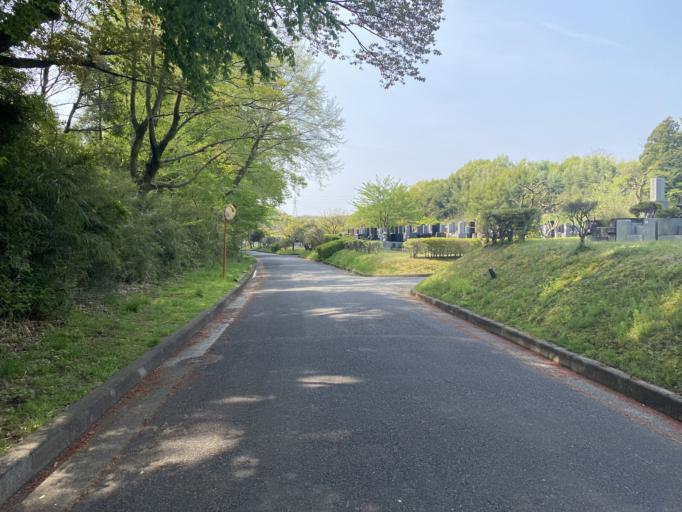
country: JP
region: Tokyo
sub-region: Machida-shi
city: Machida
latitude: 35.5746
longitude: 139.5193
